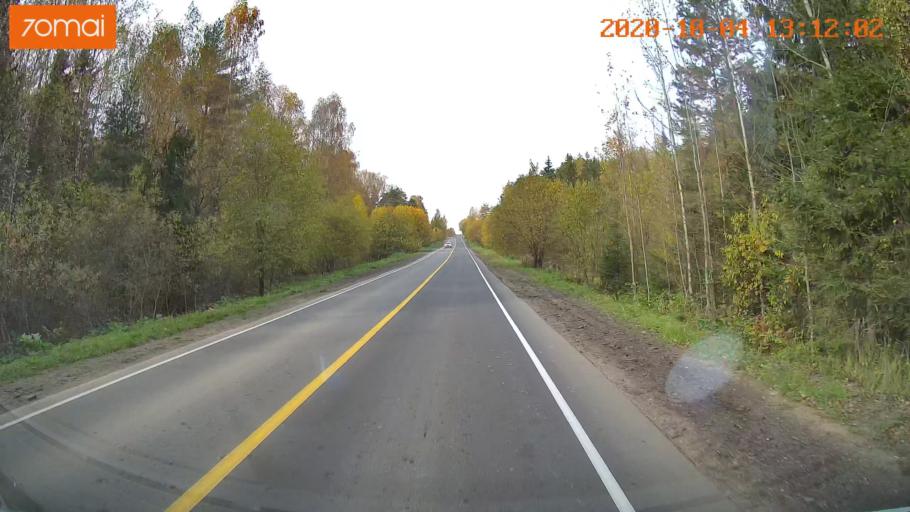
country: RU
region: Ivanovo
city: Bogorodskoye
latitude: 57.0810
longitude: 40.9333
